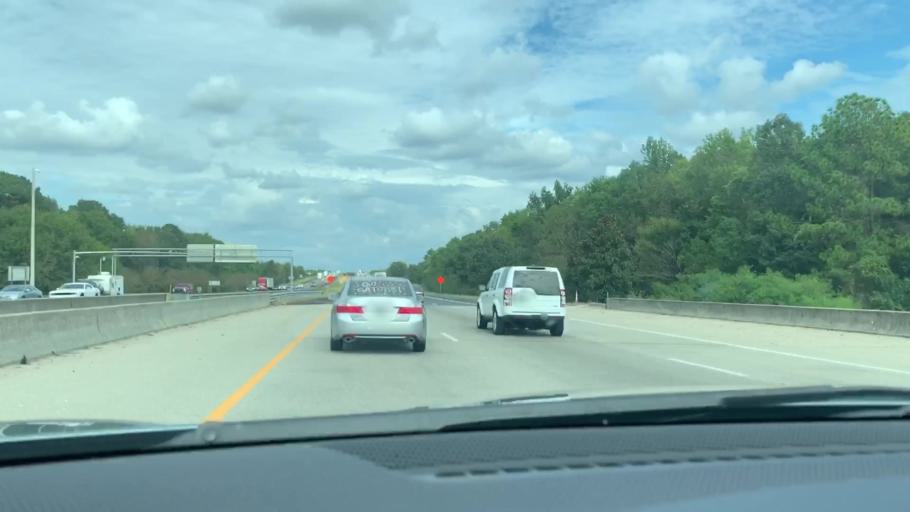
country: US
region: Georgia
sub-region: Chatham County
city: Port Wentworth
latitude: 32.2299
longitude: -81.1591
